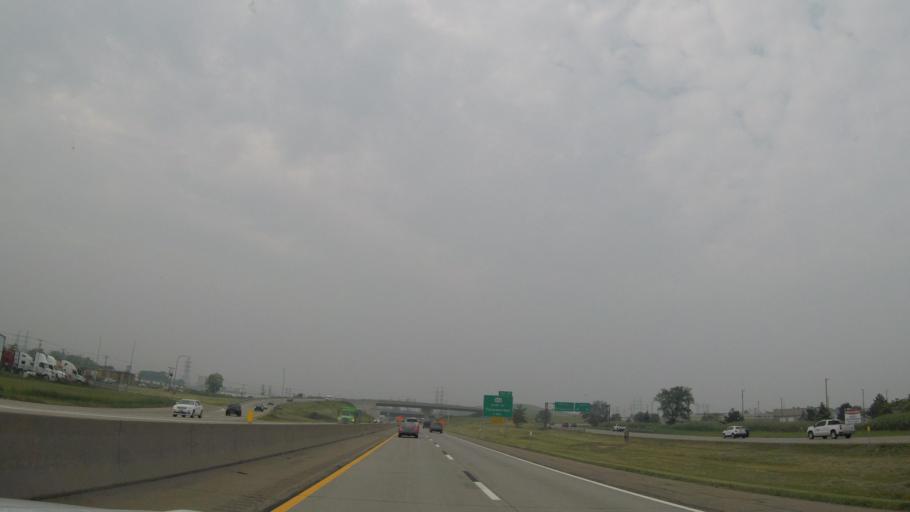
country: US
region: New York
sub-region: Erie County
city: Tonawanda
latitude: 42.9836
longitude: -78.9117
